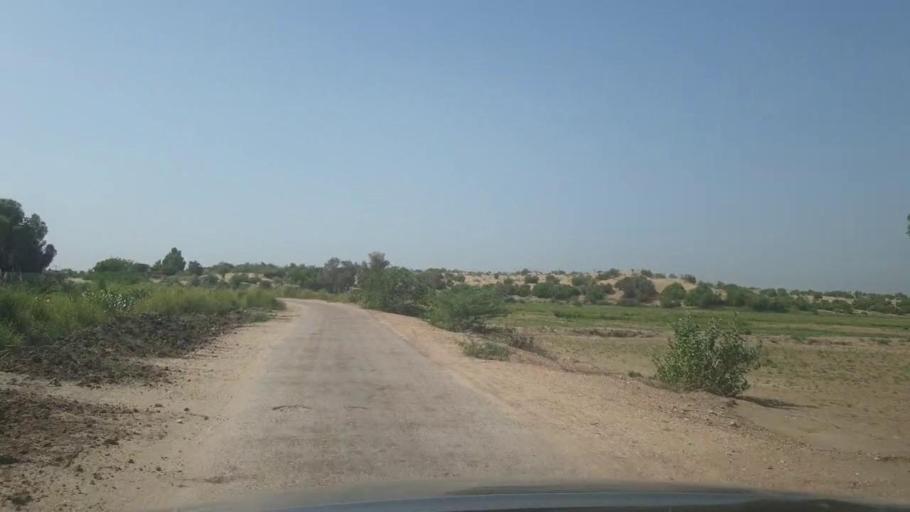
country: PK
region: Sindh
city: Rohri
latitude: 27.4321
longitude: 69.0766
